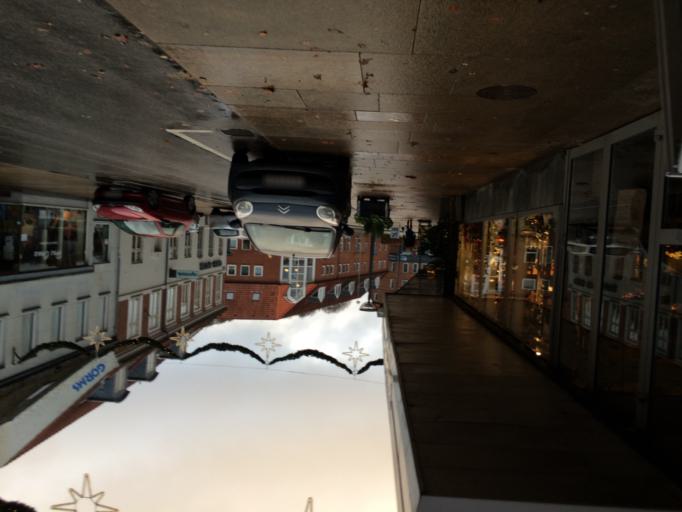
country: DK
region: South Denmark
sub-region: Vejle Kommune
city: Vejle
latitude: 55.7136
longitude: 9.5368
